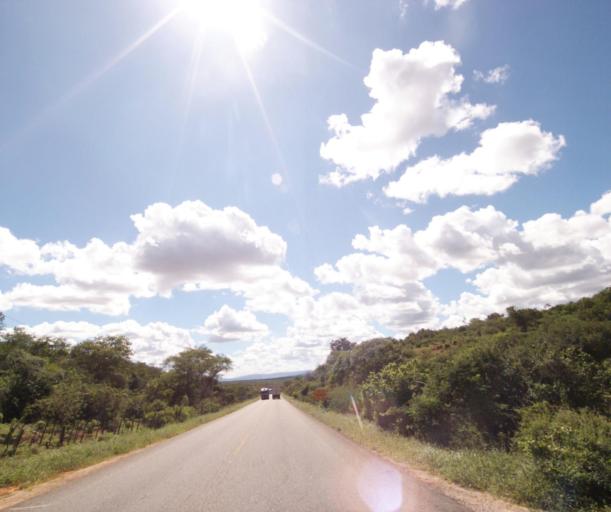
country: BR
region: Bahia
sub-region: Caetite
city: Caetite
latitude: -14.1719
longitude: -42.2158
